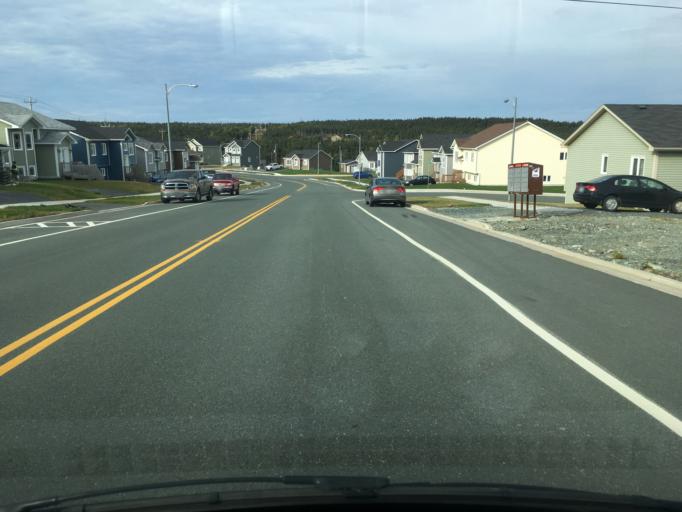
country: CA
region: Newfoundland and Labrador
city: Mount Pearl
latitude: 47.5535
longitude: -52.7910
